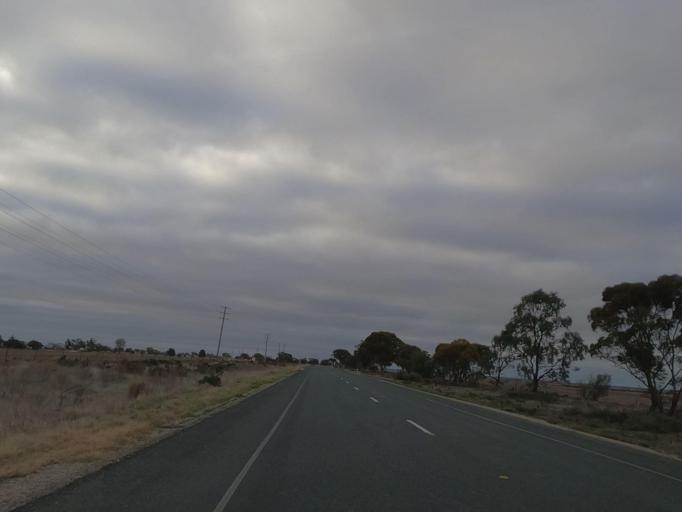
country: AU
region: Victoria
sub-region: Swan Hill
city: Swan Hill
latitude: -35.5883
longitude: 143.7904
